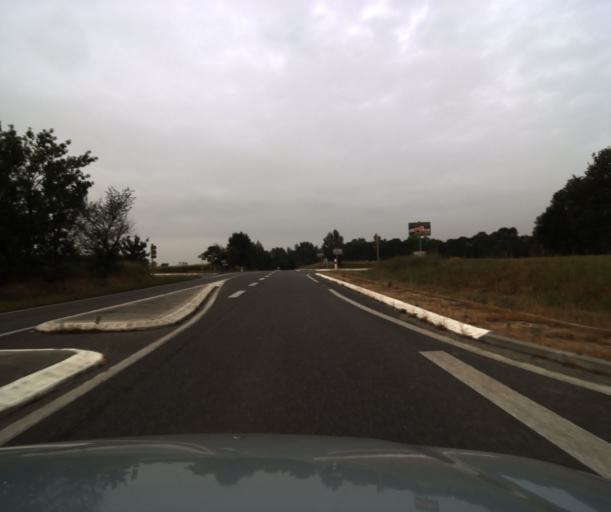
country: FR
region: Midi-Pyrenees
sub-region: Departement du Gers
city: Aubiet
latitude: 43.6897
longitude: 0.8265
